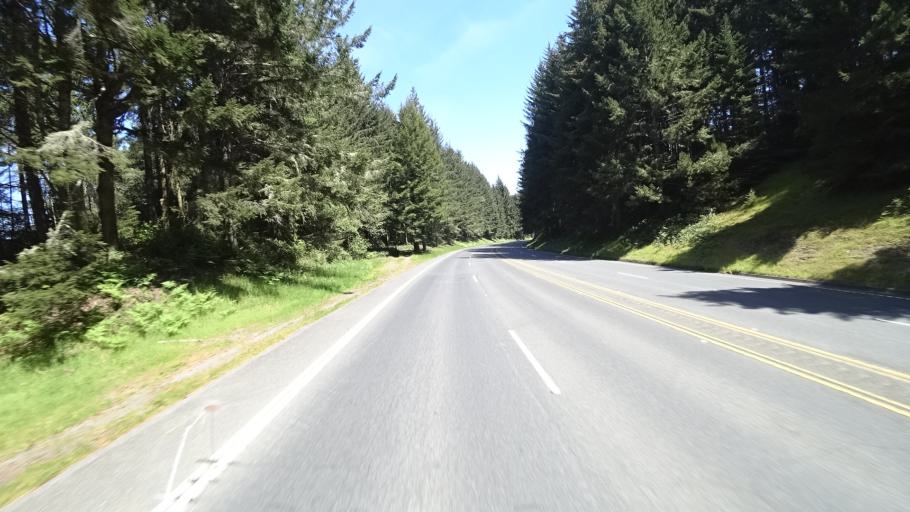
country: US
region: California
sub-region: Humboldt County
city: Westhaven-Moonstone
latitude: 41.1509
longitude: -124.1350
